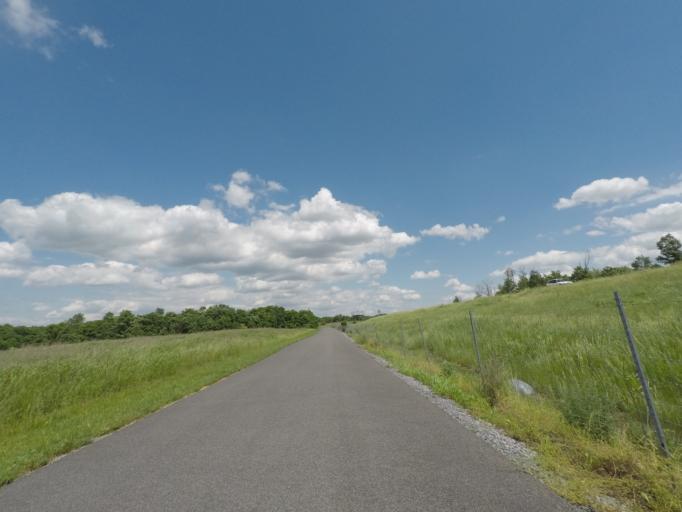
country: US
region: West Virginia
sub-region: Berkeley County
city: Martinsburg
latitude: 39.4327
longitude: -77.9540
